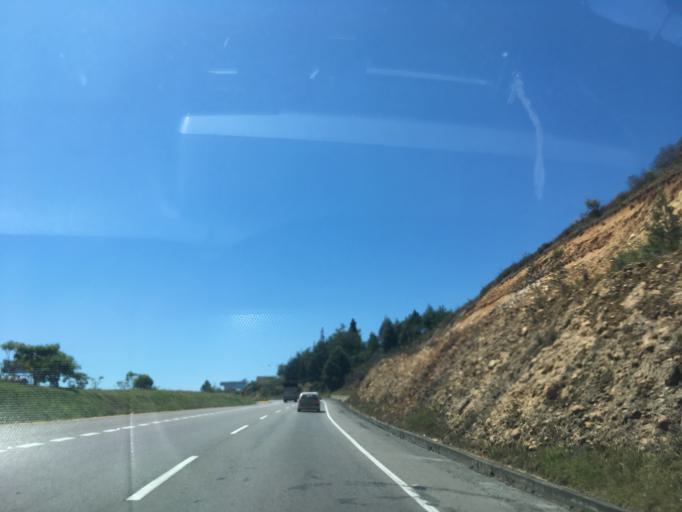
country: CO
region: Boyaca
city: Tuta
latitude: 5.6960
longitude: -73.2488
